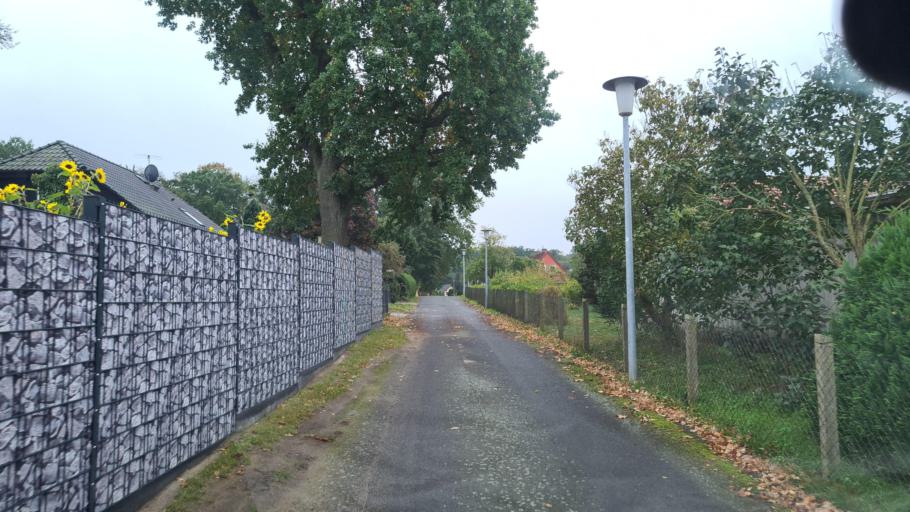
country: DE
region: Brandenburg
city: Furstenwalde
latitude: 52.4032
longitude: 14.0365
